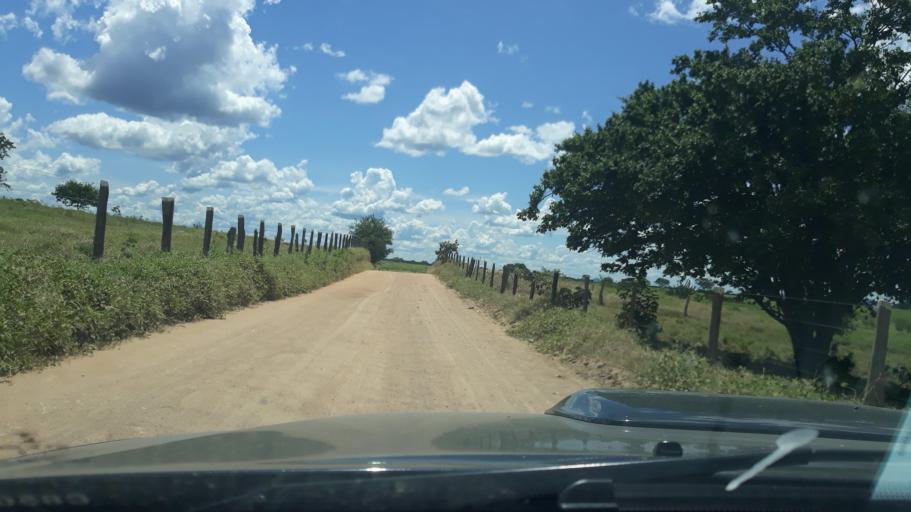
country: BR
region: Bahia
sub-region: Riacho De Santana
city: Riacho de Santana
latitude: -13.9039
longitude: -42.8623
